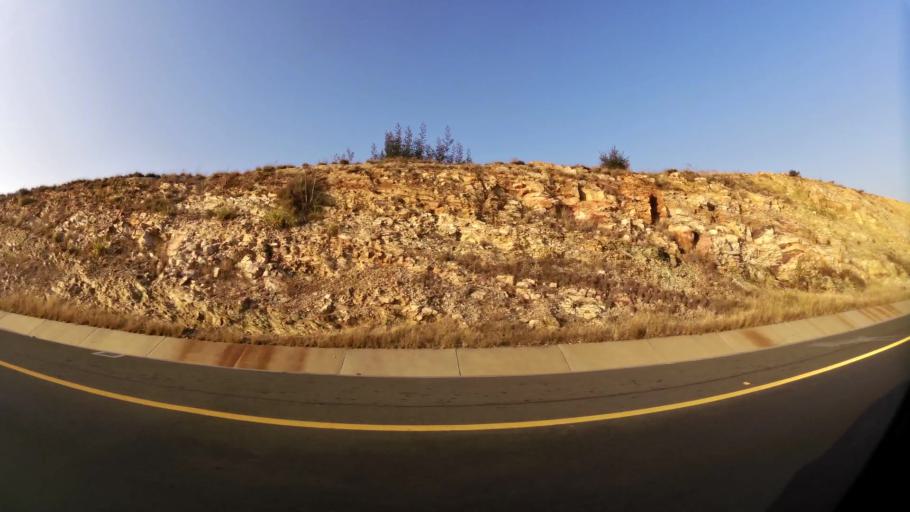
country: ZA
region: Gauteng
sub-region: City of Johannesburg Metropolitan Municipality
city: Roodepoort
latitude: -26.2192
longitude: 27.9415
